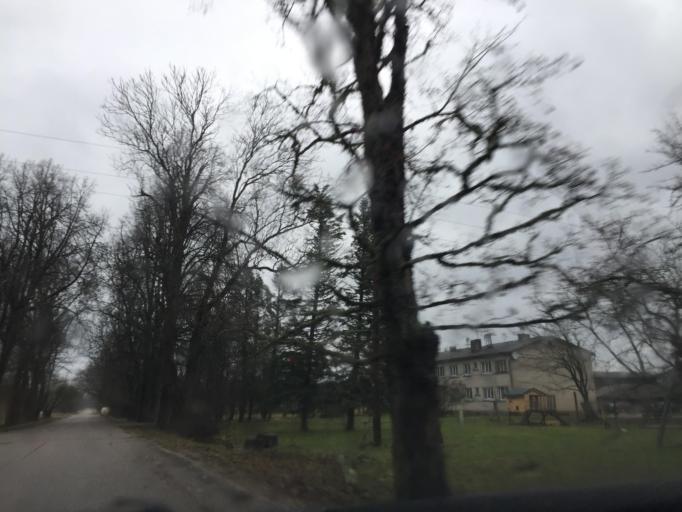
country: LV
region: Aloja
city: Aloja
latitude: 57.6618
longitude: 24.7784
